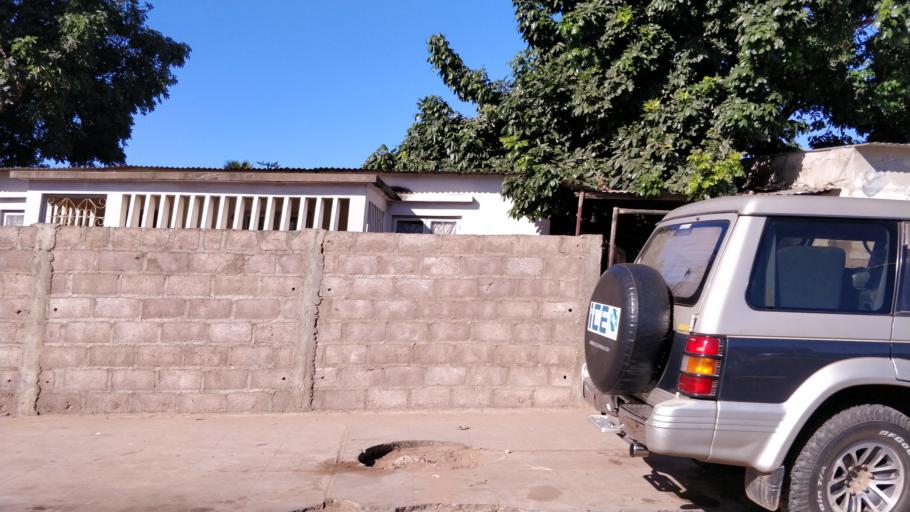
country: MZ
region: Maputo City
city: Maputo
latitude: -25.9286
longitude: 32.5988
